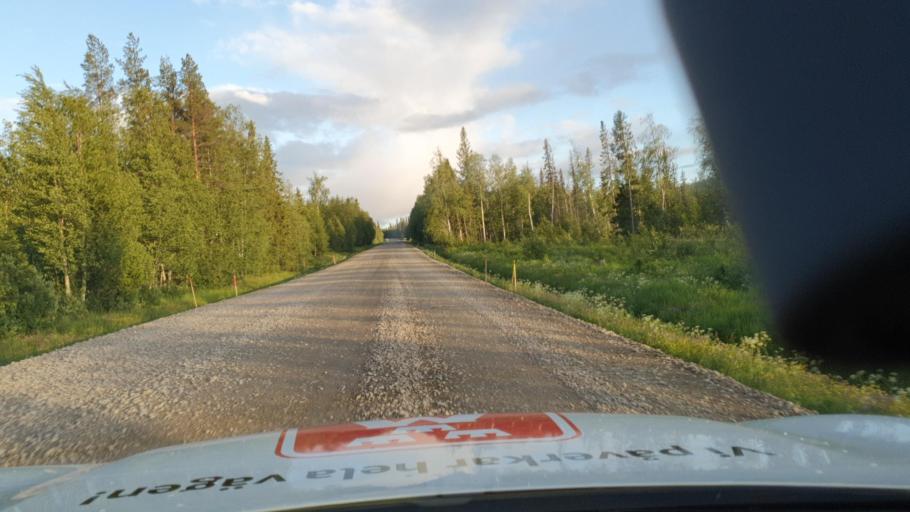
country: SE
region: Vaesterbotten
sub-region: Lycksele Kommun
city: Soderfors
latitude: 64.6678
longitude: 17.8377
